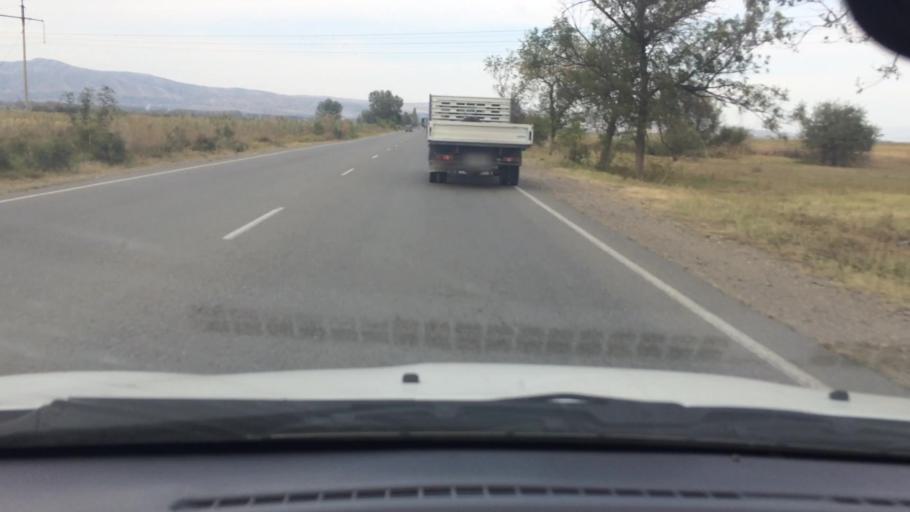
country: GE
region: Kvemo Kartli
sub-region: Marneuli
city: Marneuli
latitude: 41.5433
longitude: 44.7768
